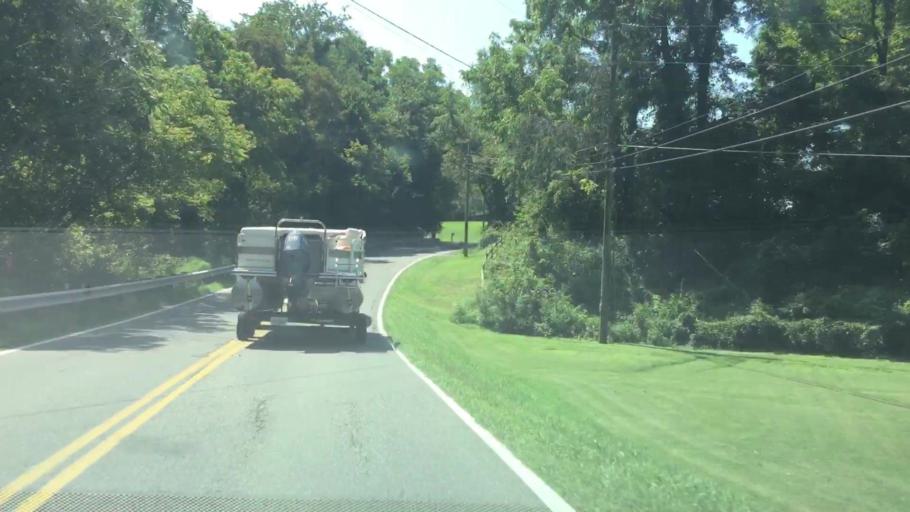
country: US
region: Virginia
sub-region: Washington County
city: Abingdon
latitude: 36.6470
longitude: -81.9858
